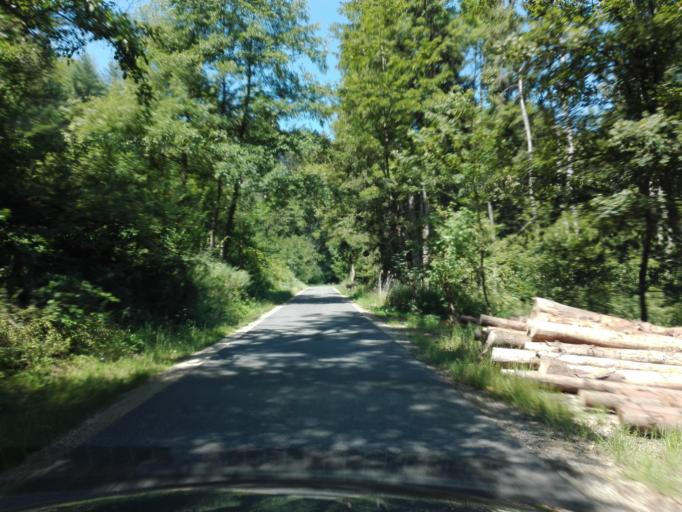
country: AT
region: Upper Austria
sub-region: Politischer Bezirk Urfahr-Umgebung
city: Steyregg
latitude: 48.3060
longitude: 14.3907
